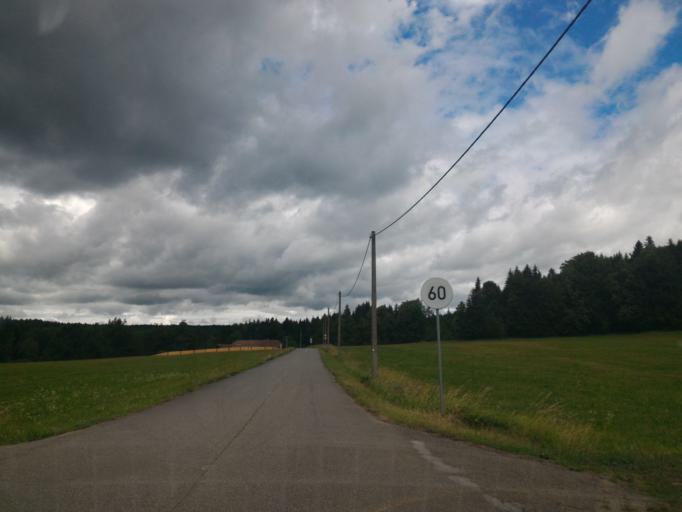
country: CZ
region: Vysocina
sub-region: Okres Jihlava
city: Telc
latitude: 49.2433
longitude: 15.4280
